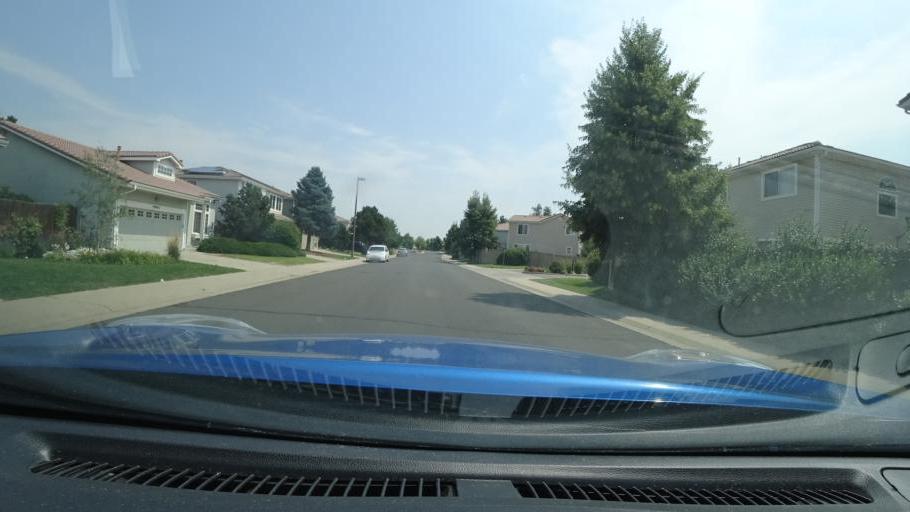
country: US
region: Colorado
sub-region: Adams County
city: Aurora
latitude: 39.7764
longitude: -104.7559
